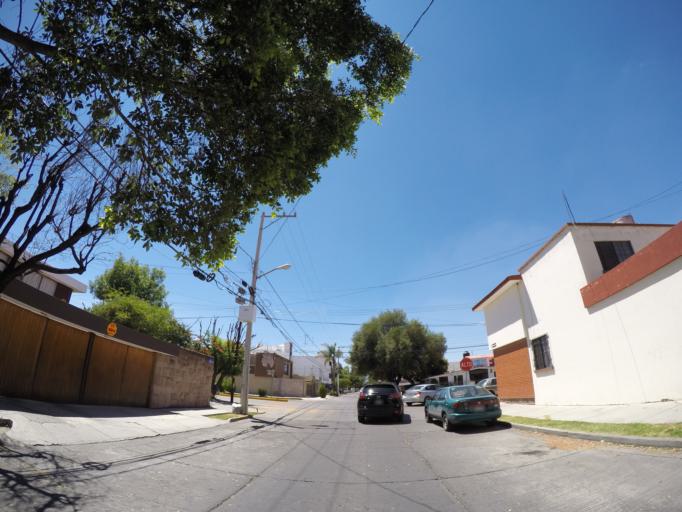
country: MX
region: San Luis Potosi
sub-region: San Luis Potosi
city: San Luis Potosi
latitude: 22.1424
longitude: -101.0030
